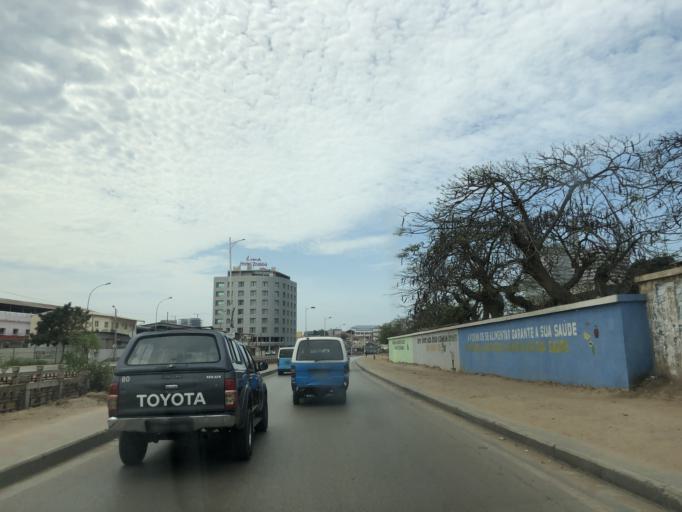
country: AO
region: Luanda
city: Luanda
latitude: -8.8300
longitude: 13.2553
